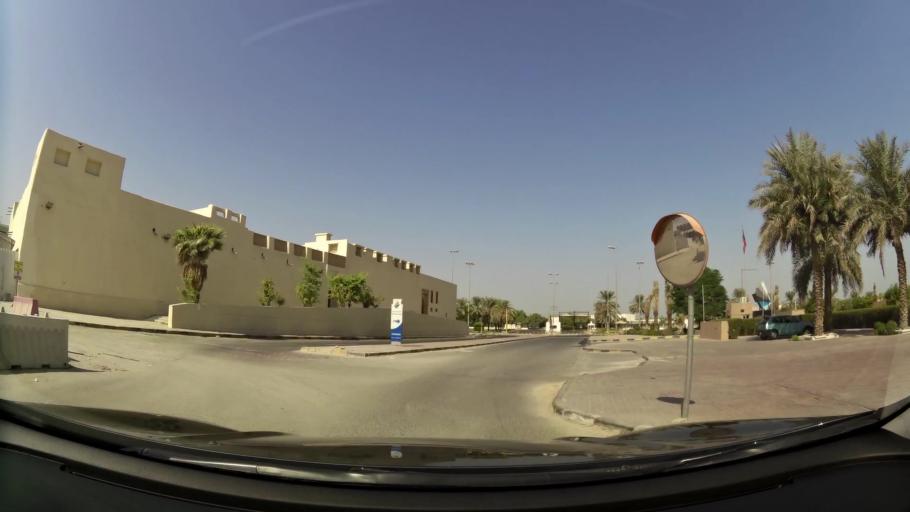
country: KW
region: Al Asimah
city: Kuwait City
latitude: 29.3745
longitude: 47.9679
